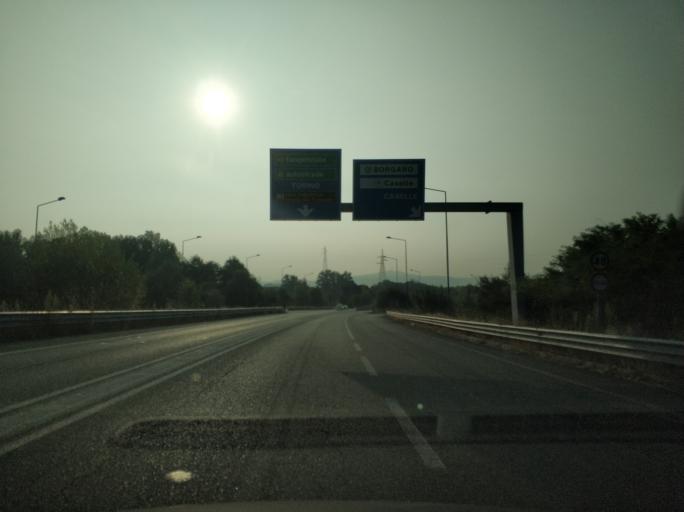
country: IT
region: Piedmont
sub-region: Provincia di Torino
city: Borgaro Torinese
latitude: 45.1476
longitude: 7.6461
